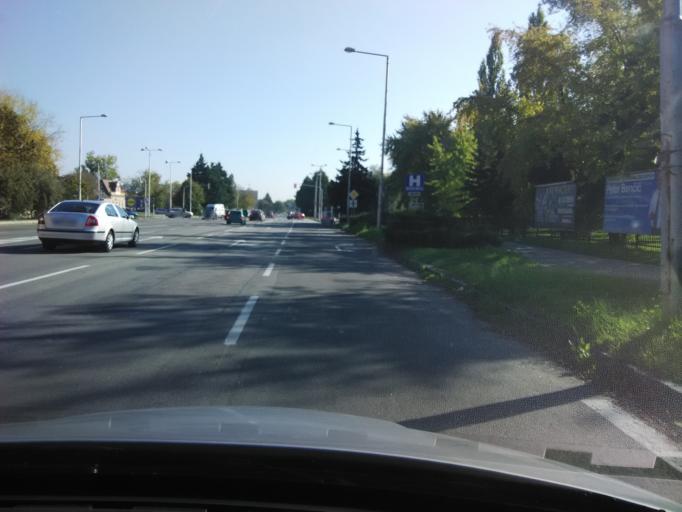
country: SK
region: Nitriansky
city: Komarno
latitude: 47.7645
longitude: 18.1242
